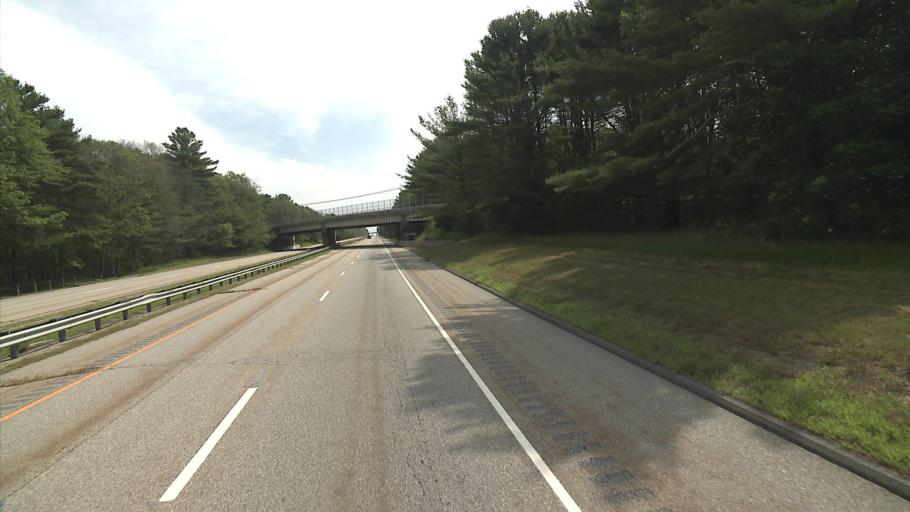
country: US
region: Connecticut
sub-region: Windham County
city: Danielson
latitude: 41.7783
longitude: -71.8406
